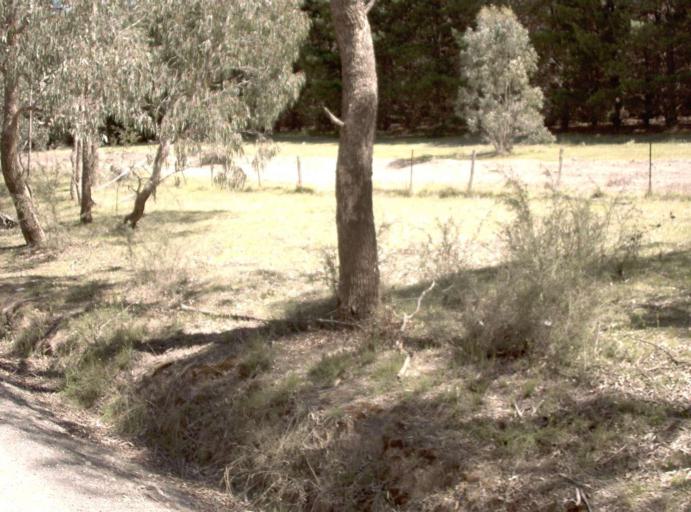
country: AU
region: New South Wales
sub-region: Bombala
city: Bombala
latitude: -37.1164
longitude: 148.6519
